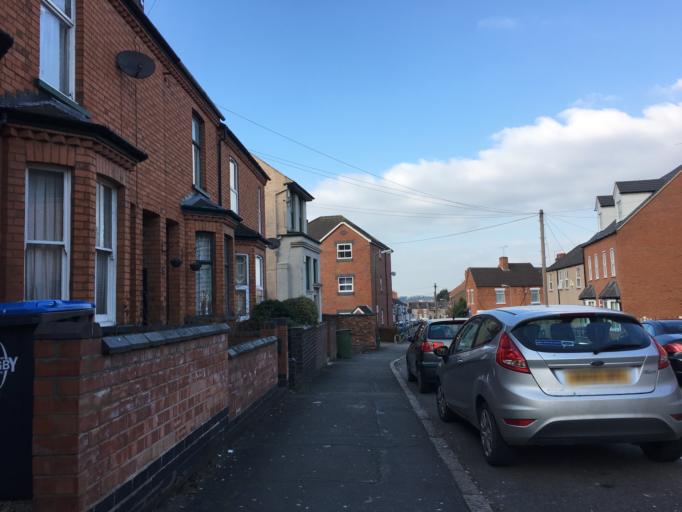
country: GB
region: England
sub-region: Warwickshire
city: Rugby
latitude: 52.3763
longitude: -1.2577
